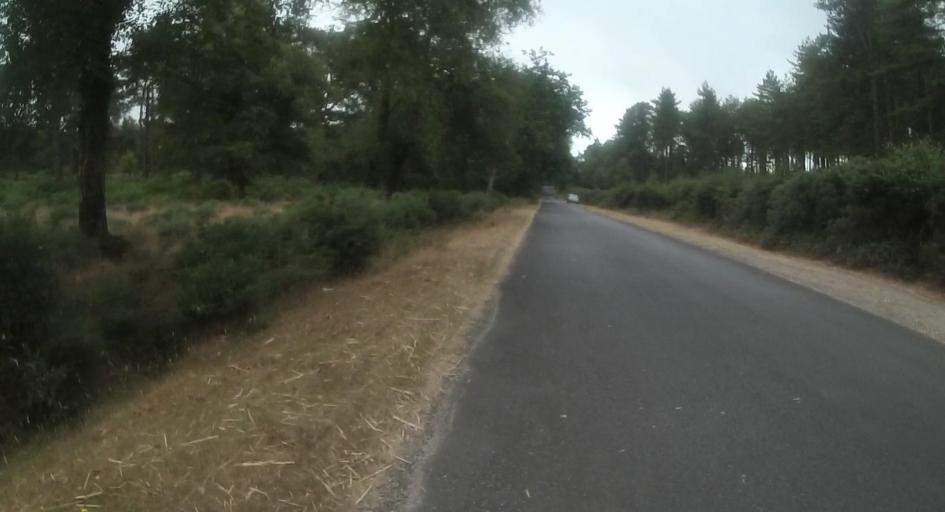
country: GB
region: England
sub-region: Dorset
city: Bovington Camp
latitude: 50.7221
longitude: -2.2553
